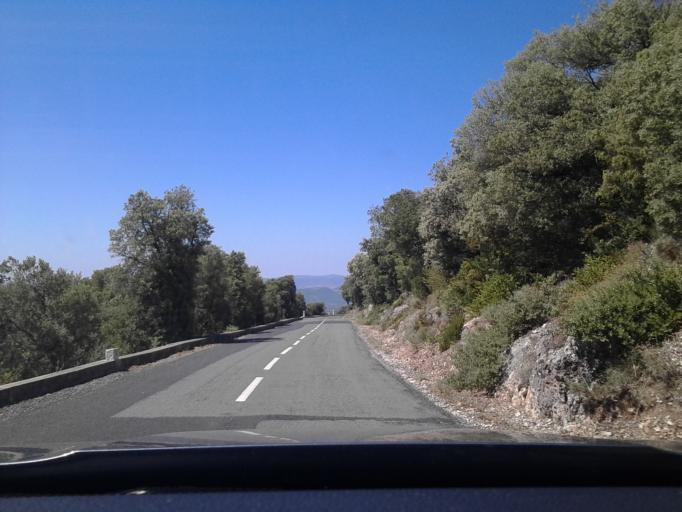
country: FR
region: Languedoc-Roussillon
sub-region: Departement de l'Herault
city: Montpeyroux
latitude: 43.7360
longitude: 3.4547
